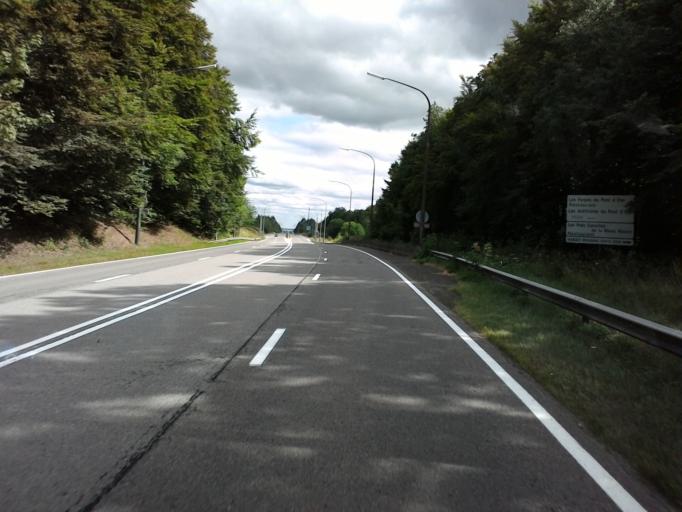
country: BE
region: Wallonia
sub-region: Province du Luxembourg
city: Martelange
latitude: 49.7895
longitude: 5.7430
